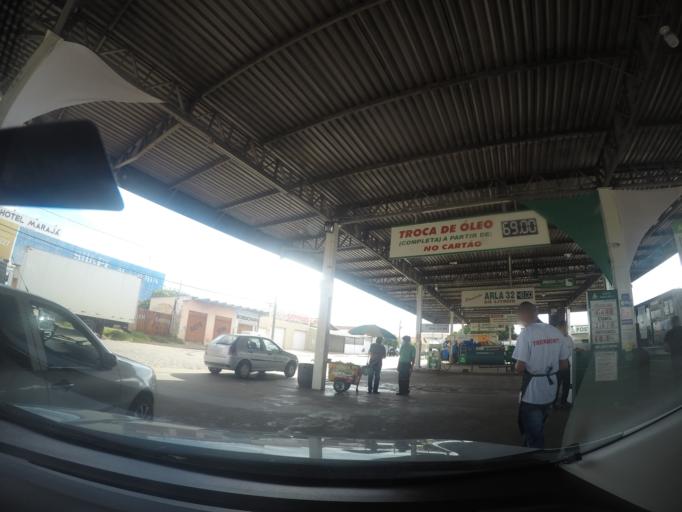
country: BR
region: Goias
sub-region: Goiania
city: Goiania
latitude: -16.6735
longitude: -49.3061
